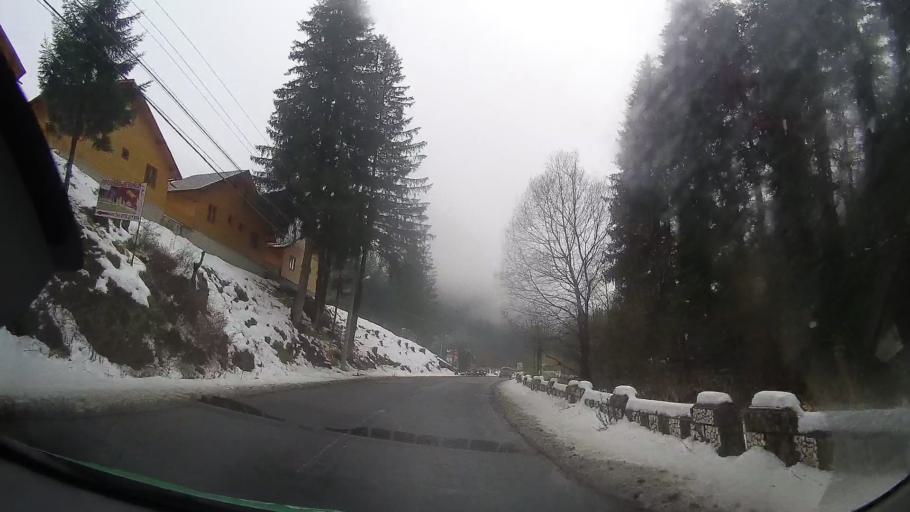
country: RO
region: Neamt
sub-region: Comuna Bicaz Chei
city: Bicaz Chei
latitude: 46.7972
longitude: 25.8020
